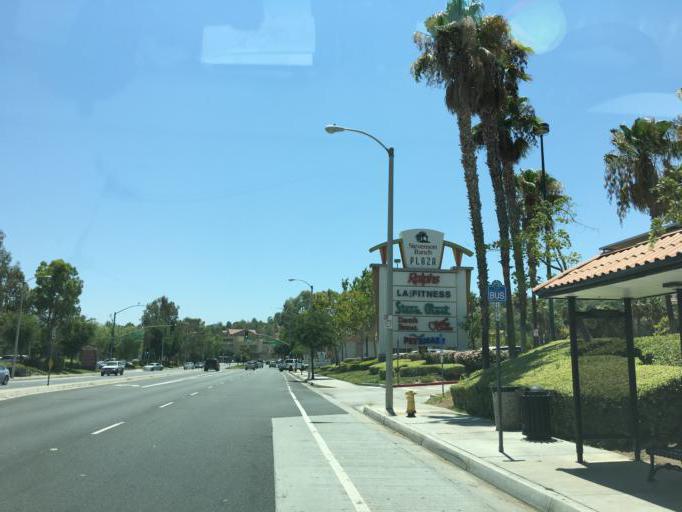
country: US
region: California
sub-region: Los Angeles County
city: Santa Clarita
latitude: 34.3837
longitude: -118.5716
